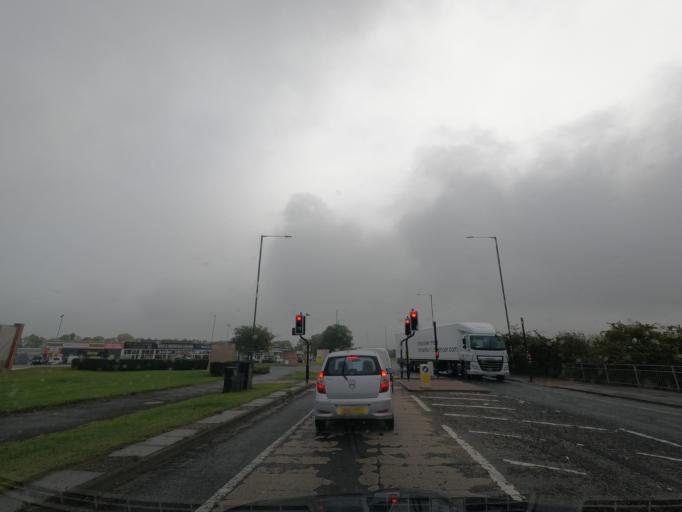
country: GB
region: England
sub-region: Redcar and Cleveland
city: South Bank
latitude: 54.5690
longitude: -1.1773
